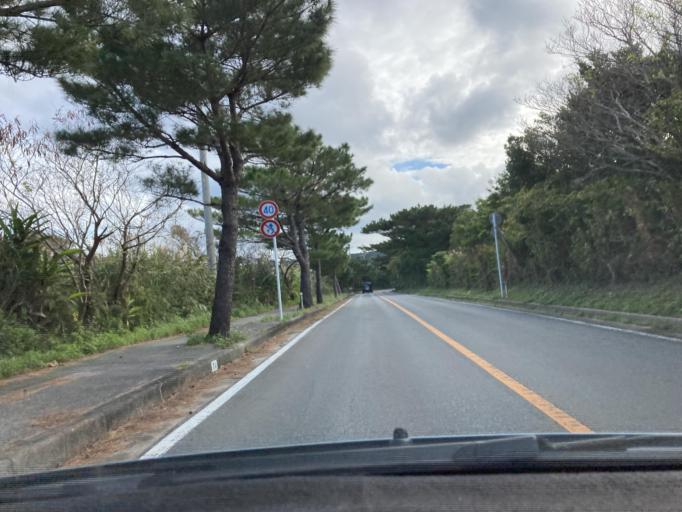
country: JP
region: Okinawa
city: Nago
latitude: 26.8635
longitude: 128.2595
